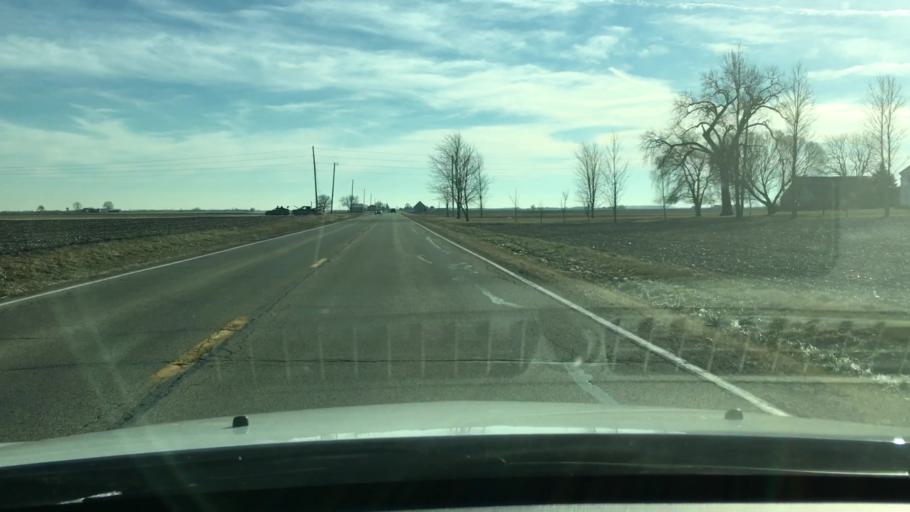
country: US
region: Illinois
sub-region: LaSalle County
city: Peru
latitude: 41.4270
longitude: -89.1265
